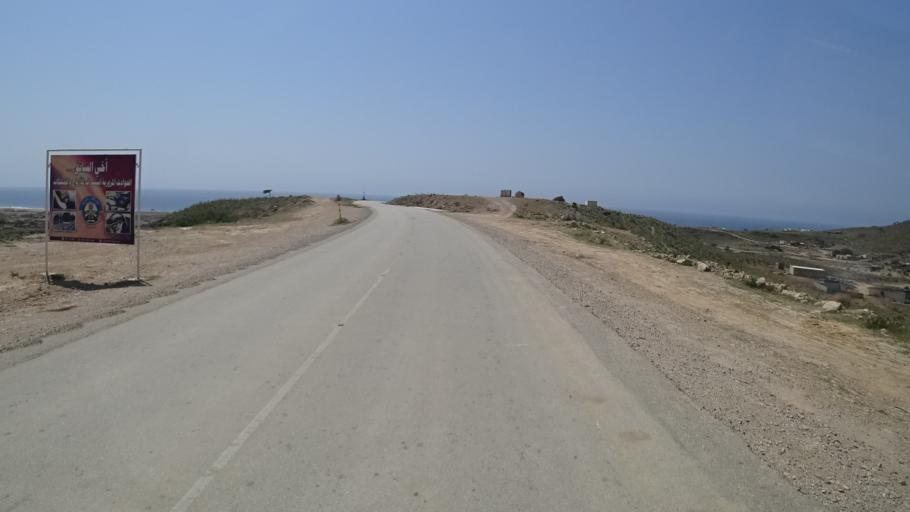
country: OM
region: Zufar
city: Salalah
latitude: 17.0421
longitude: 54.6127
